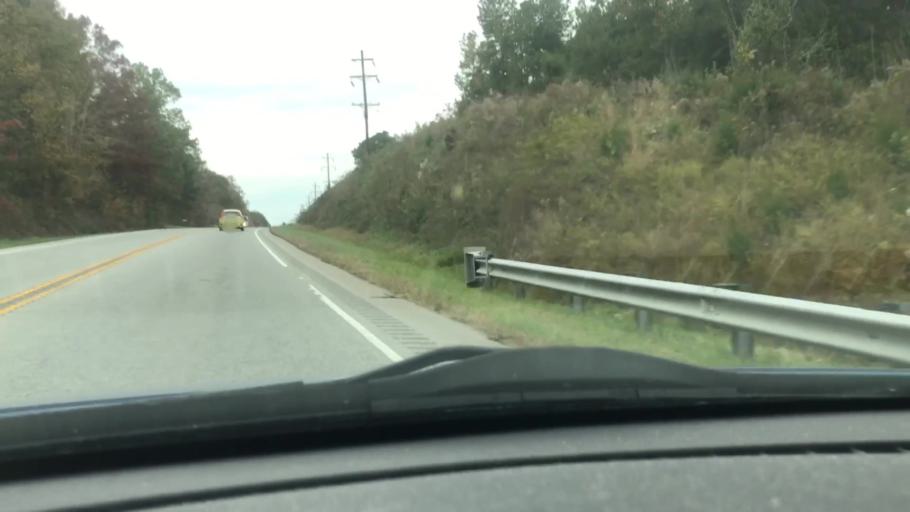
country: US
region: North Carolina
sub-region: Davidson County
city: Thomasville
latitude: 35.7536
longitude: -80.0401
